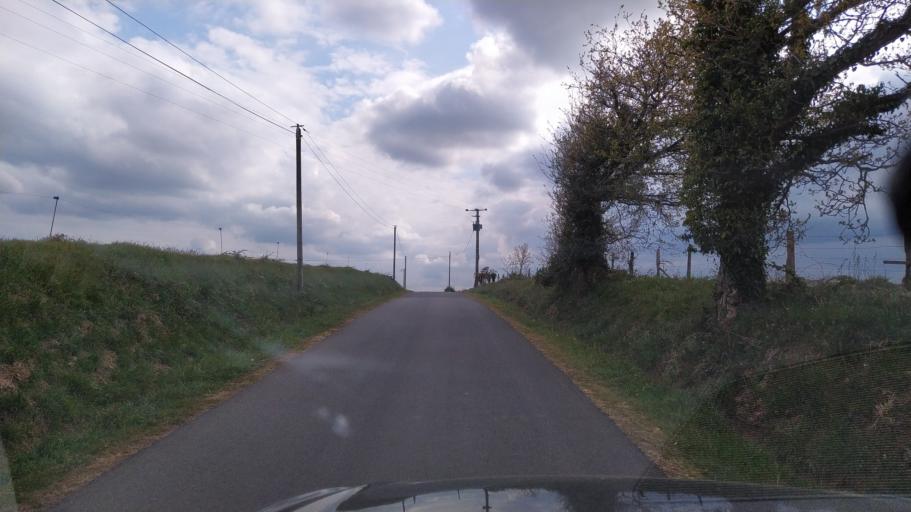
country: FR
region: Brittany
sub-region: Departement du Finistere
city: Bodilis
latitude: 48.5097
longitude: -4.1174
